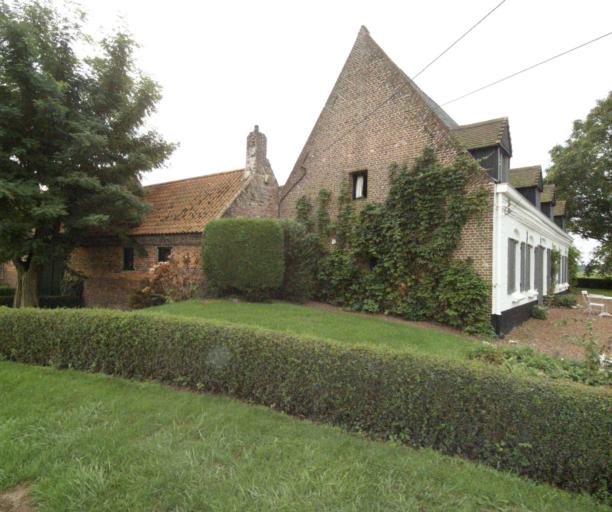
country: FR
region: Nord-Pas-de-Calais
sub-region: Departement du Nord
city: Baisieux
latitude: 50.6224
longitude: 3.2498
